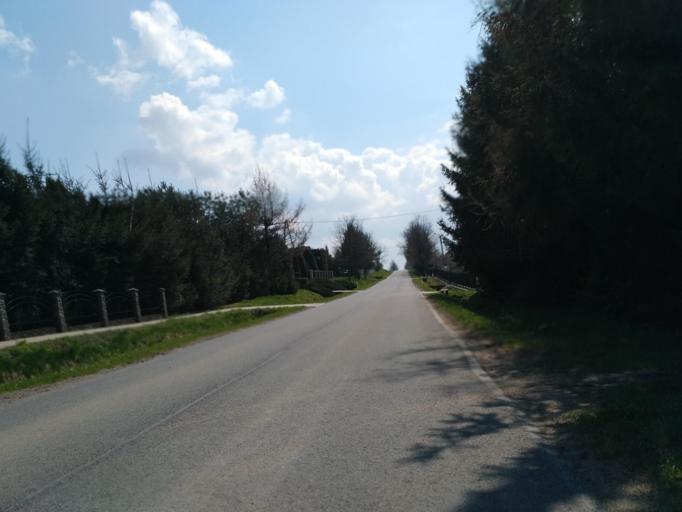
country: PL
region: Subcarpathian Voivodeship
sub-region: Powiat sanocki
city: Bukowsko
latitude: 49.5013
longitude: 22.0359
